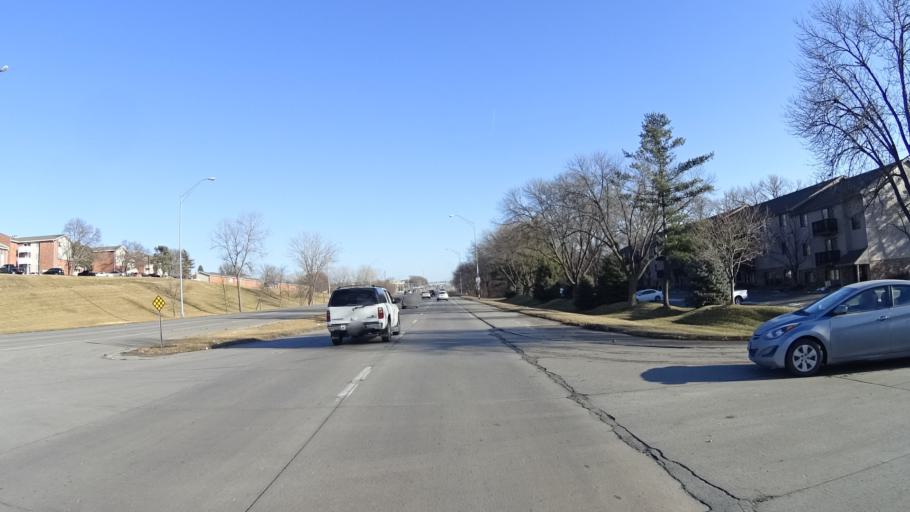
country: US
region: Nebraska
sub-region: Douglas County
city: Ralston
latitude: 41.2901
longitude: -96.0926
